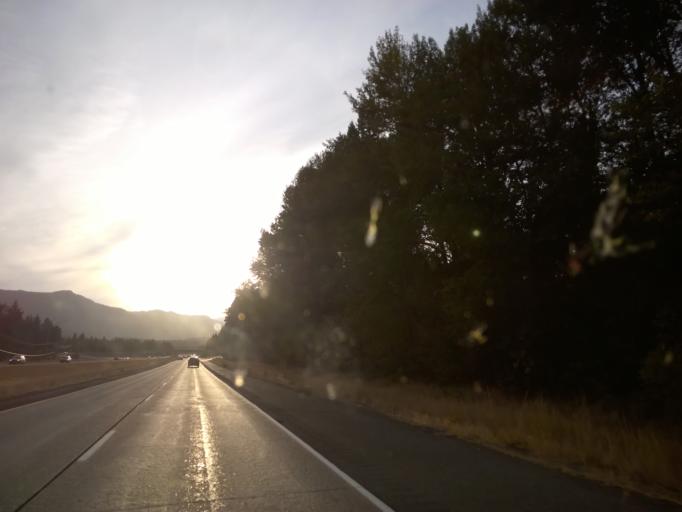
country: US
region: Washington
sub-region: Kittitas County
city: Cle Elum
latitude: 47.1843
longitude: -121.0076
